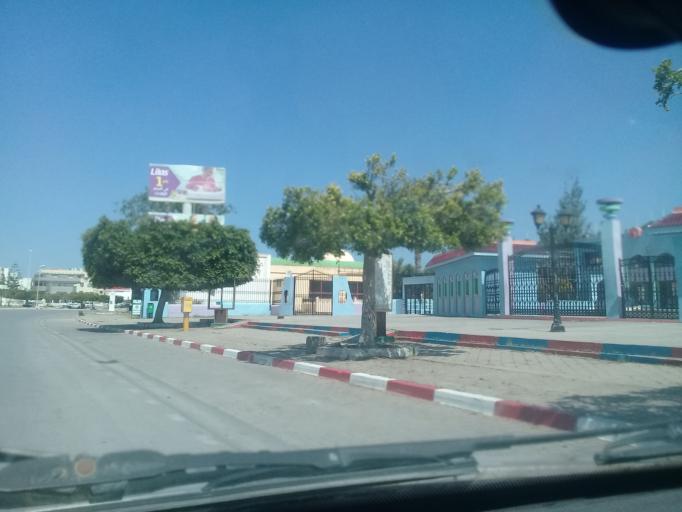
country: TN
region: Ariana
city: Ariana
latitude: 36.8343
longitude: 10.2257
